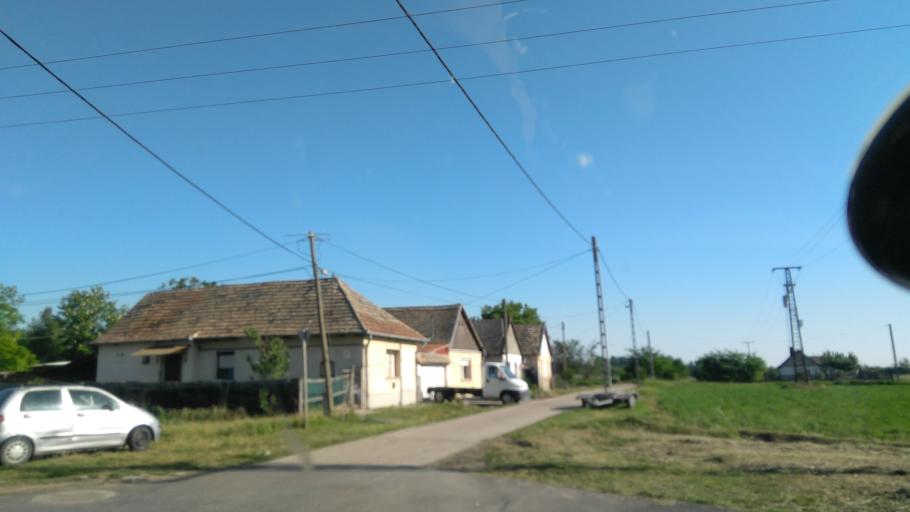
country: HU
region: Bekes
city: Elek
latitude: 46.5342
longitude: 21.2583
